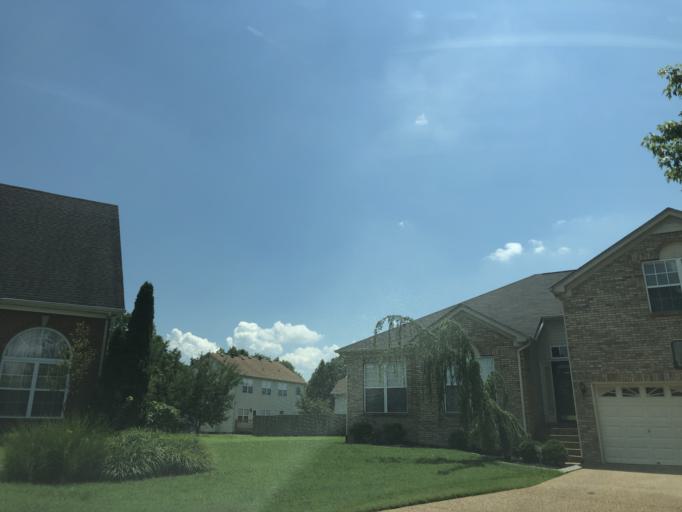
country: US
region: Tennessee
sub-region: Davidson County
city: Lakewood
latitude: 36.1785
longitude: -86.6397
